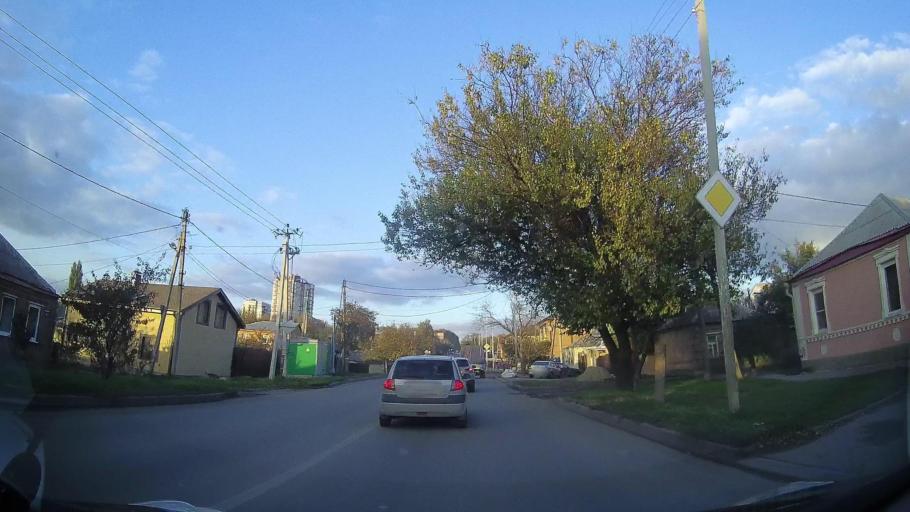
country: RU
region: Rostov
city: Imeni Chkalova
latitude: 47.2712
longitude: 39.7802
